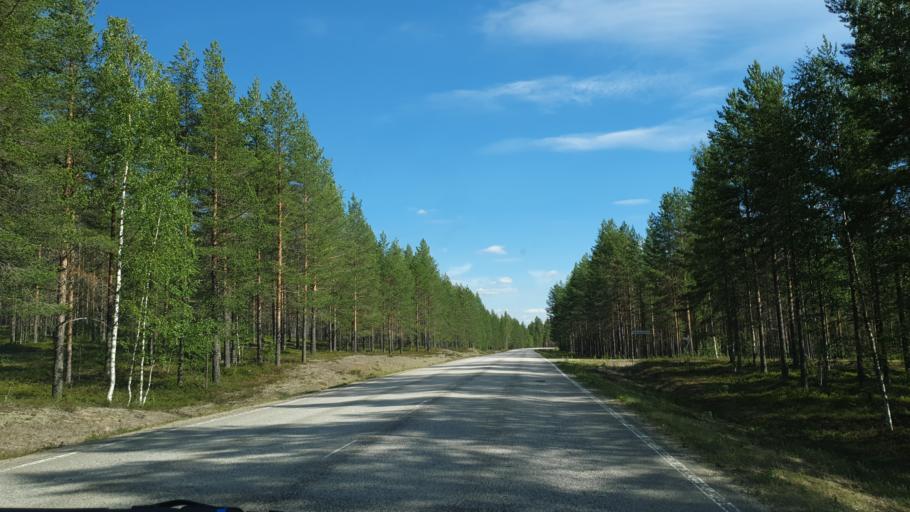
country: FI
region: Kainuu
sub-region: Kehys-Kainuu
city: Kuhmo
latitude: 64.1870
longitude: 29.2054
